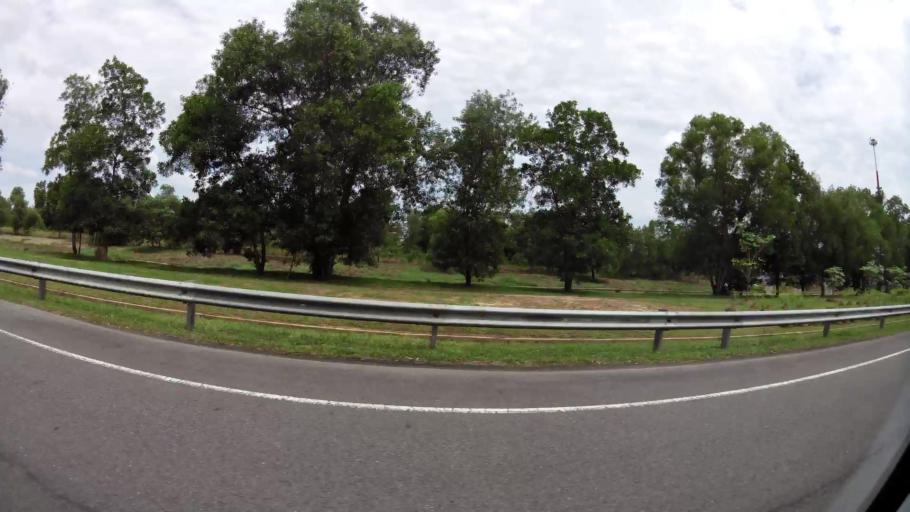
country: BN
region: Brunei and Muara
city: Bandar Seri Begawan
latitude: 4.9369
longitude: 114.9332
